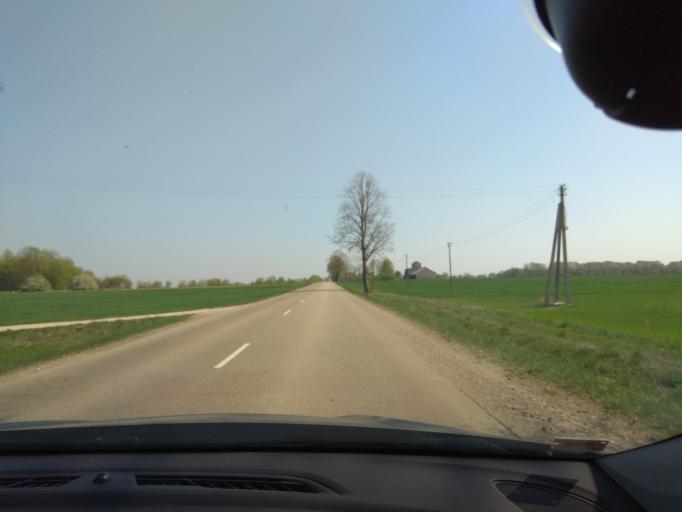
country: LT
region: Panevezys
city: Pasvalys
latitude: 55.9406
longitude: 24.2252
